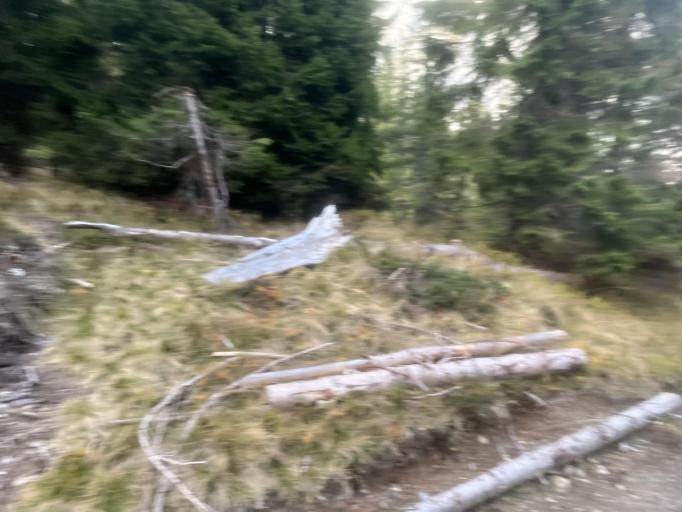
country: IT
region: Veneto
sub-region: Provincia di Belluno
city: Granvilla
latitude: 46.6235
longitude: 12.7065
